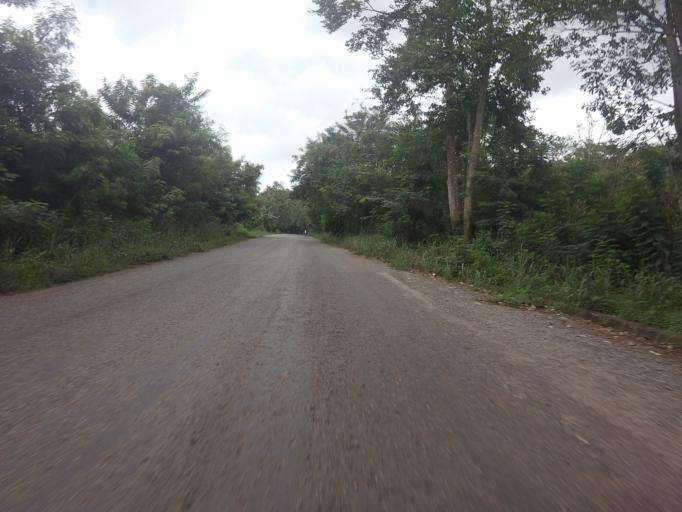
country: GH
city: Akropong
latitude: 5.9584
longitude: -0.1219
